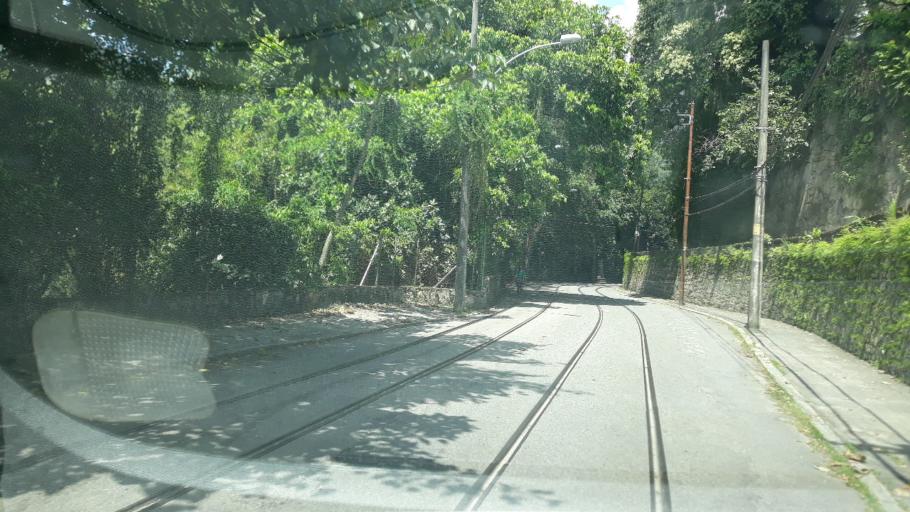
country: BR
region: Rio de Janeiro
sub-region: Rio De Janeiro
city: Rio de Janeiro
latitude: -22.9374
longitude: -43.2037
